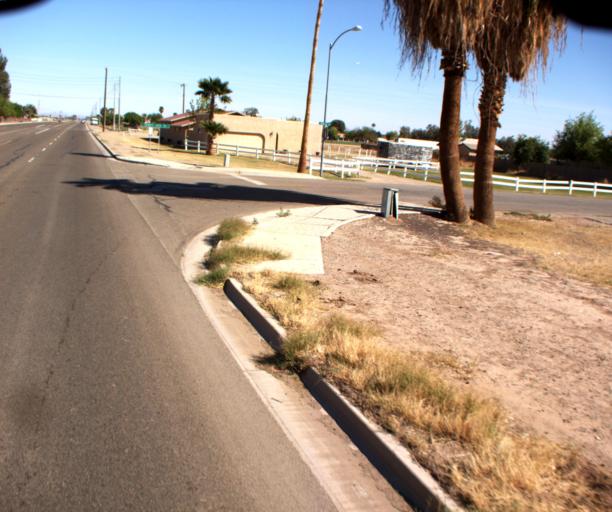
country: US
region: Arizona
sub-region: Yuma County
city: Somerton
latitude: 32.6390
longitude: -114.6500
